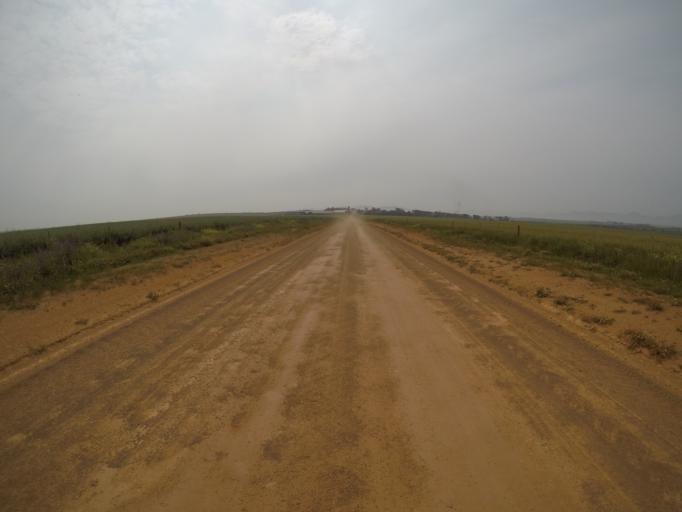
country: ZA
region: Western Cape
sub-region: City of Cape Town
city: Kraaifontein
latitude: -33.7120
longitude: 18.6861
